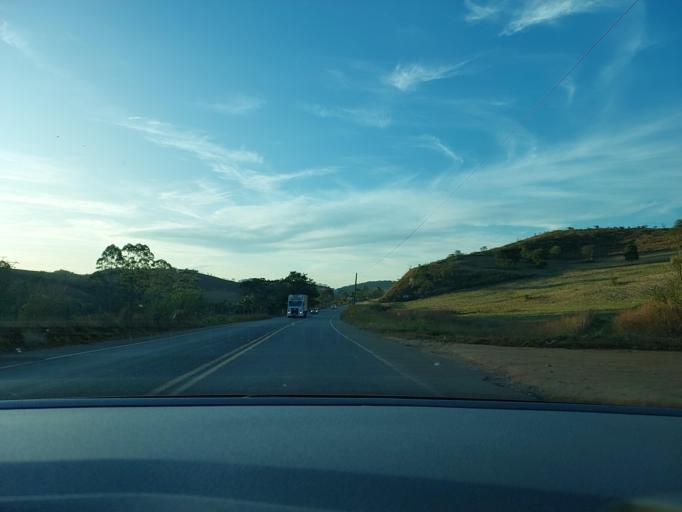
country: BR
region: Minas Gerais
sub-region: Vicosa
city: Vicosa
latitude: -20.7975
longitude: -42.8369
